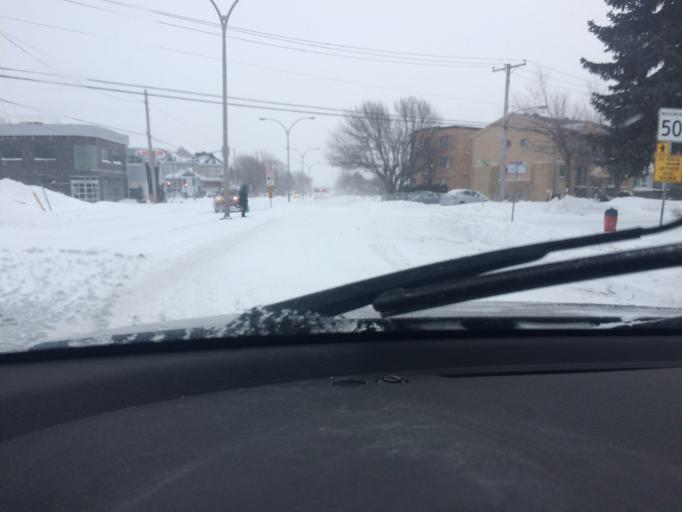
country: CA
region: Quebec
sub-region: Monteregie
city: Brossard
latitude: 45.4680
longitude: -73.4624
